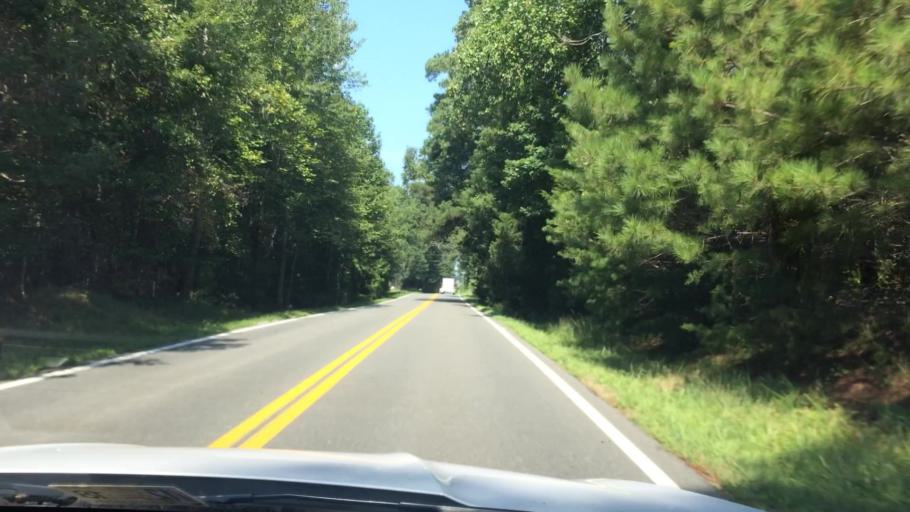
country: US
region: Virginia
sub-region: New Kent County
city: New Kent
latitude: 37.5195
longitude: -76.9990
